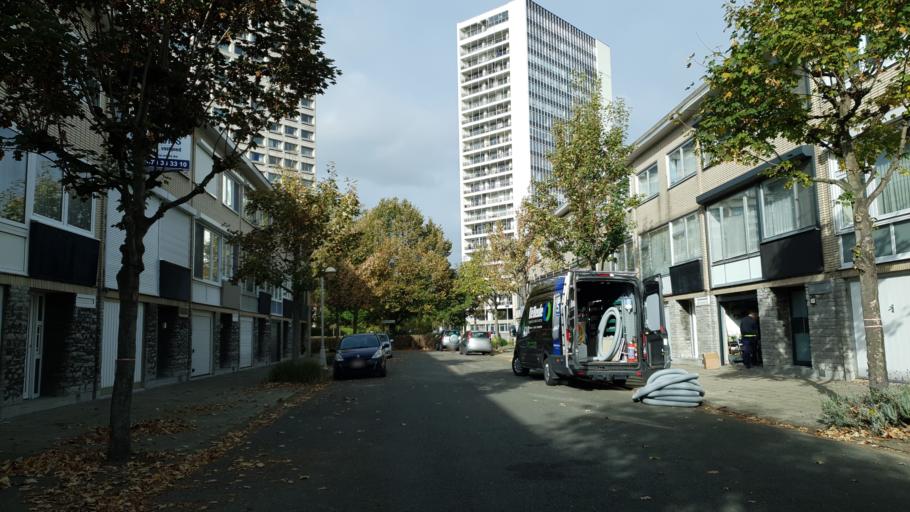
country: BE
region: Flanders
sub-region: Provincie Antwerpen
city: Antwerpen
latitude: 51.2317
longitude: 4.3854
